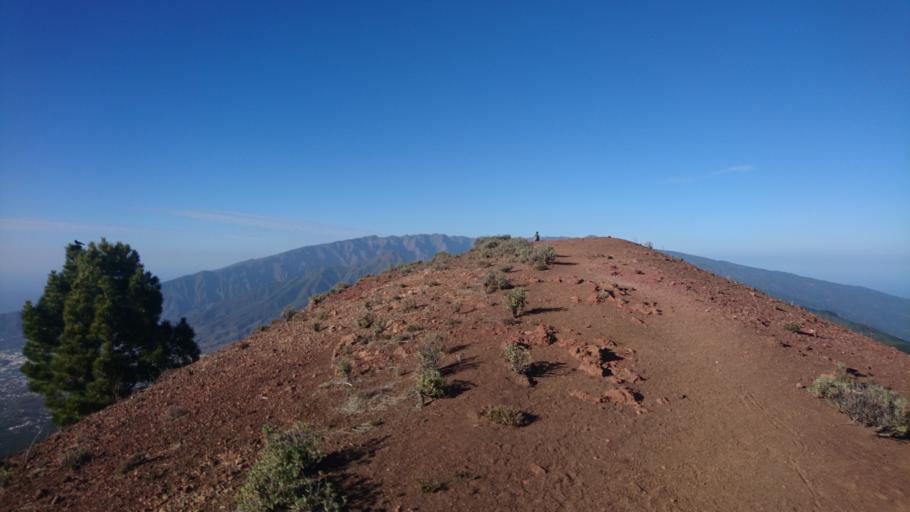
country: ES
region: Canary Islands
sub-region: Provincia de Santa Cruz de Tenerife
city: Brena Baja
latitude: 28.6046
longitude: -17.8408
